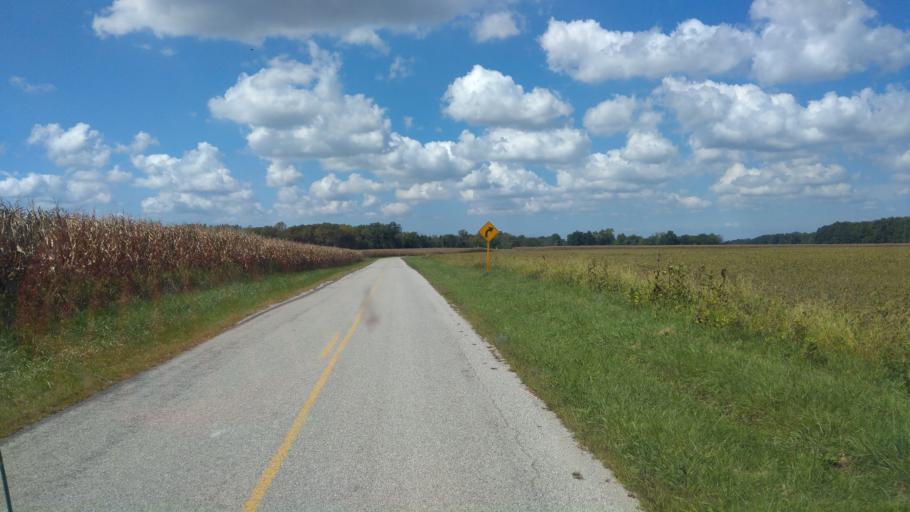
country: US
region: Ohio
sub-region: Wyandot County
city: Upper Sandusky
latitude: 40.6728
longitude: -83.3481
